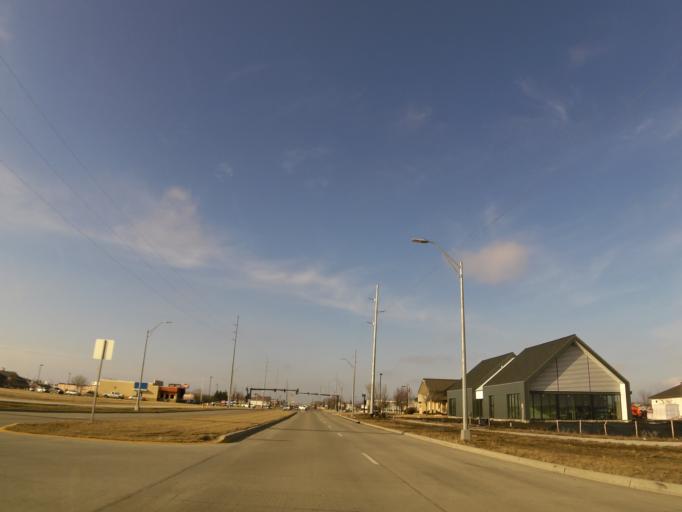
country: US
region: North Dakota
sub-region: Grand Forks County
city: Grand Forks
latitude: 47.8839
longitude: -97.0667
